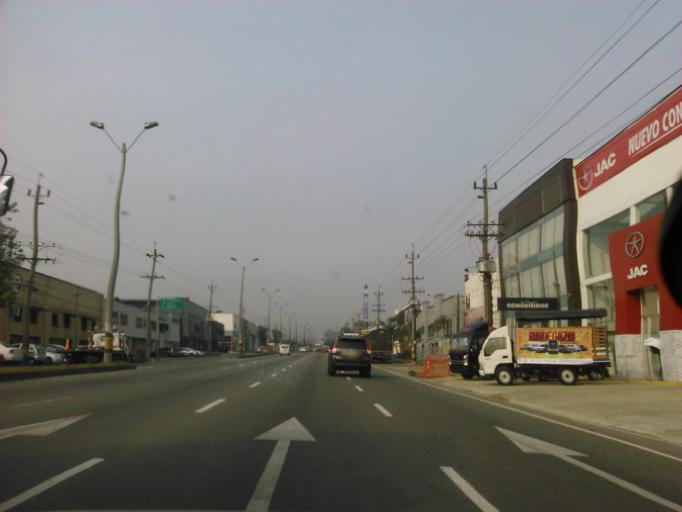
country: CO
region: Antioquia
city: Sabaneta
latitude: 6.1640
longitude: -75.6124
